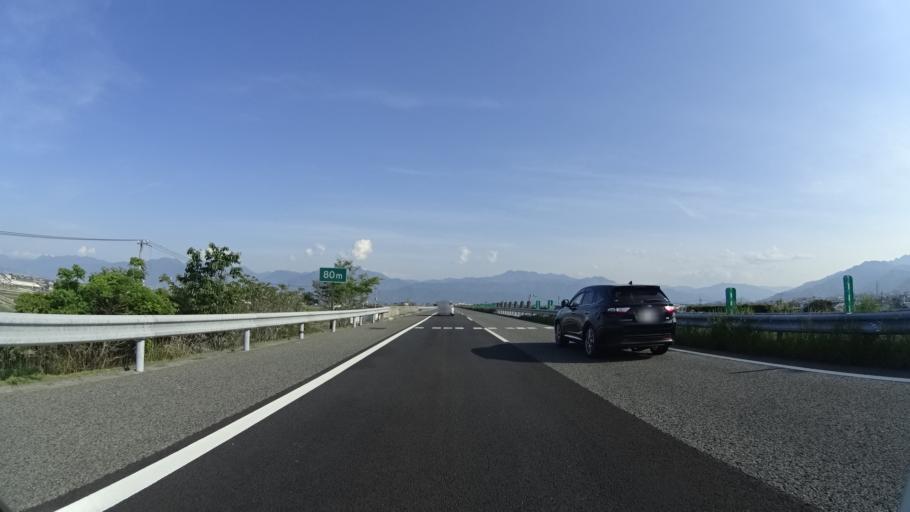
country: JP
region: Ehime
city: Saijo
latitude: 33.9609
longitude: 133.0645
